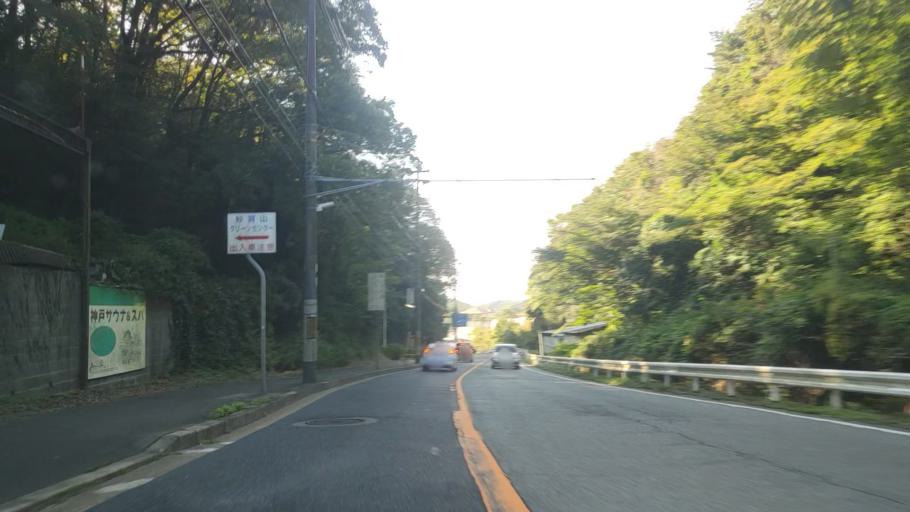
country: JP
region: Hyogo
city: Kobe
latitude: 34.7325
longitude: 135.1592
